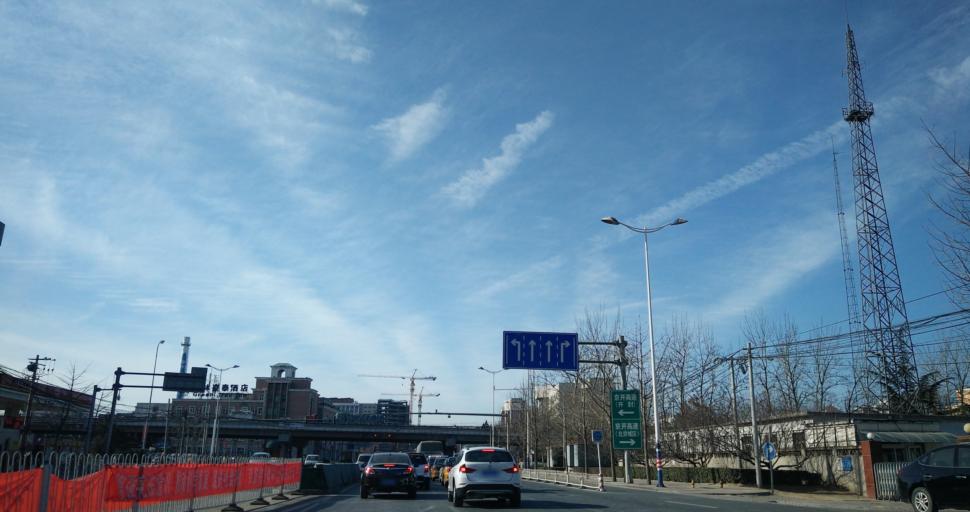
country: CN
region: Beijing
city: Xingfeng
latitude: 39.7413
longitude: 116.3406
